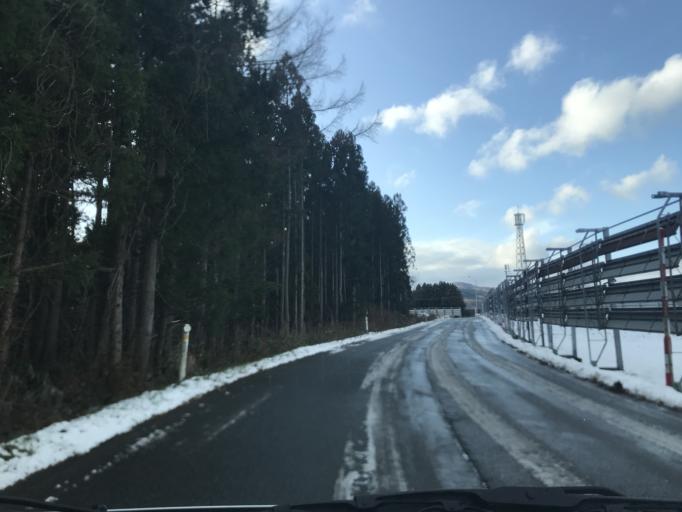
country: JP
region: Iwate
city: Kitakami
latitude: 39.2441
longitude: 140.9987
